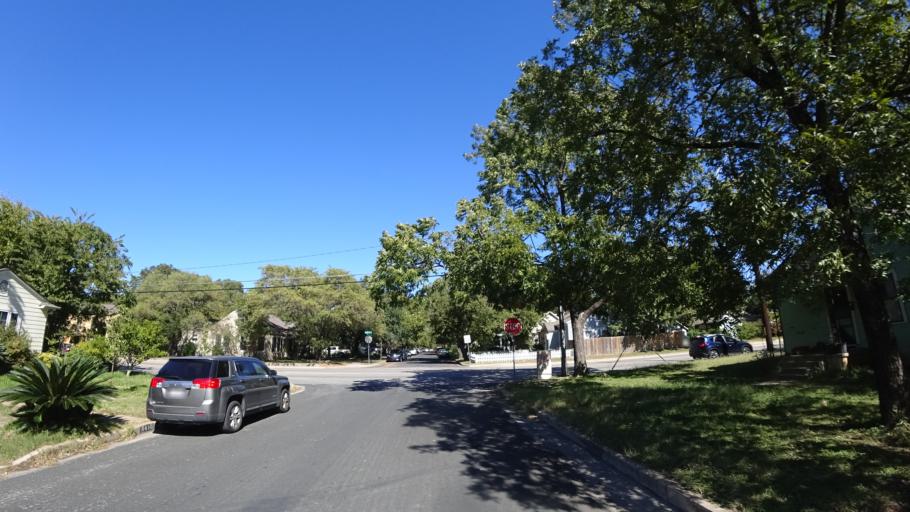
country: US
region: Texas
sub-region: Travis County
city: Austin
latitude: 30.3155
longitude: -97.7426
